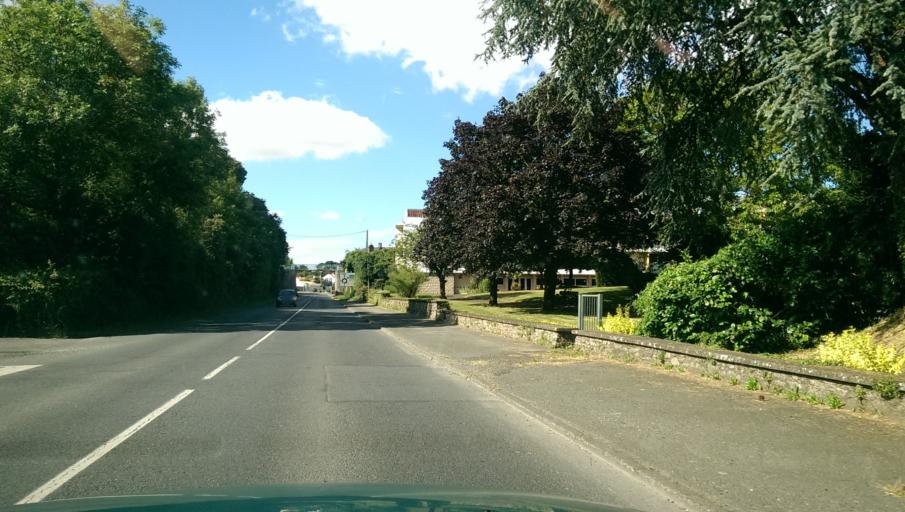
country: FR
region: Pays de la Loire
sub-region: Departement de la Vendee
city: Rocheserviere
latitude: 46.9362
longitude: -1.5143
